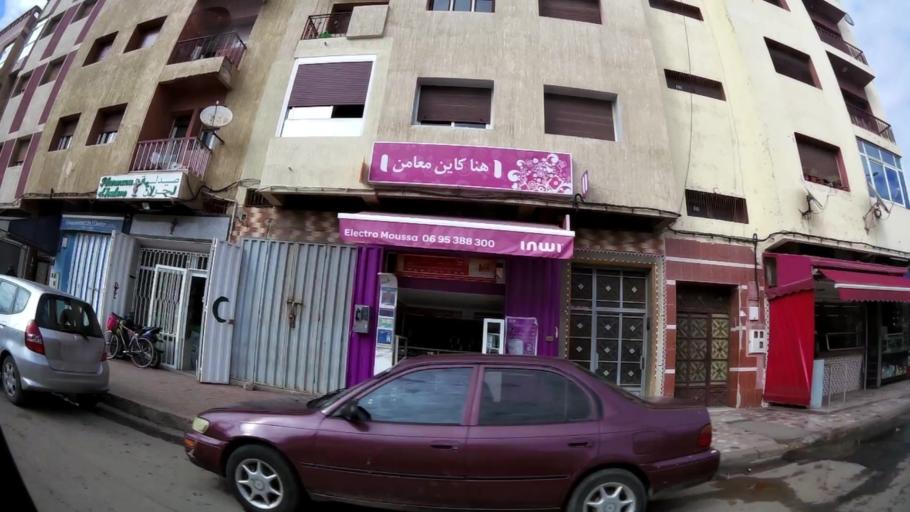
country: MA
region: Grand Casablanca
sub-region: Mohammedia
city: Mohammedia
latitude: 33.6878
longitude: -7.3772
